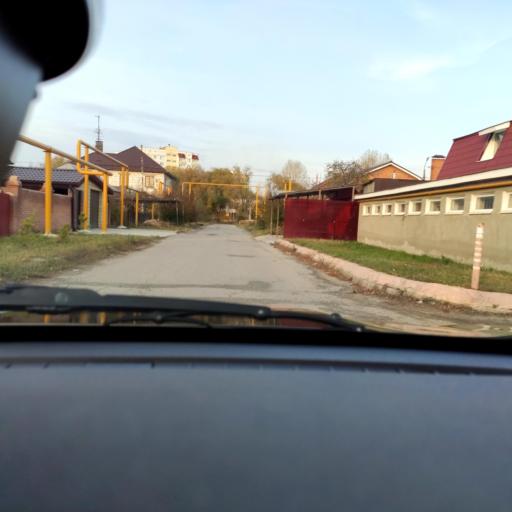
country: RU
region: Samara
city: Tol'yatti
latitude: 53.5290
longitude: 49.4280
